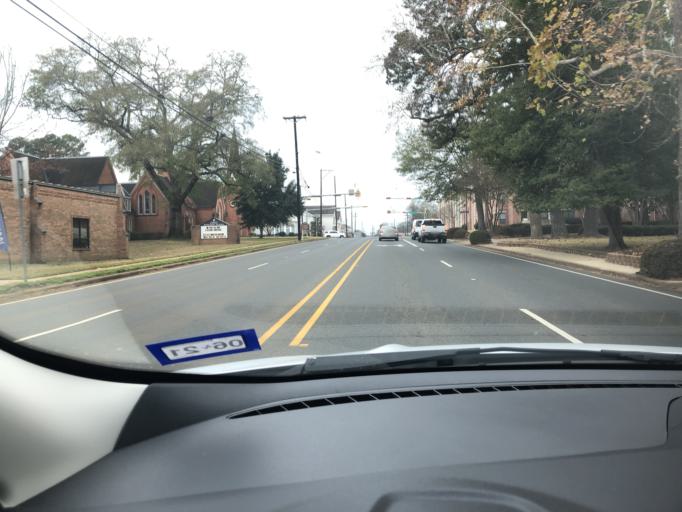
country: US
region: Texas
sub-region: Nacogdoches County
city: Nacogdoches
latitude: 31.6160
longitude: -94.6482
